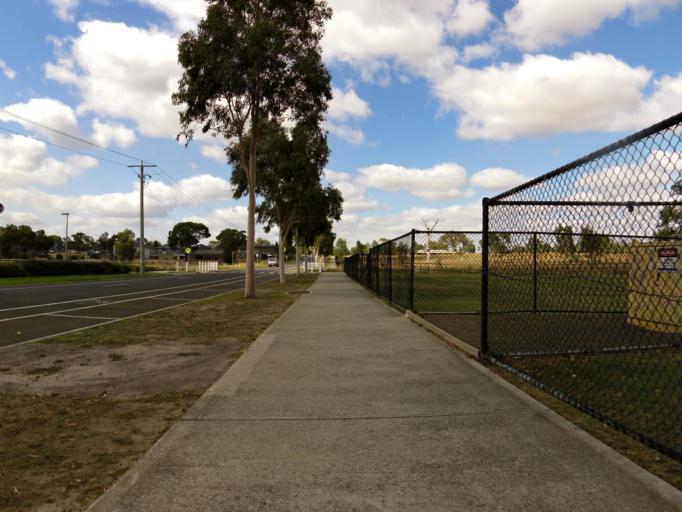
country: AU
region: Victoria
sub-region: Whittlesea
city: Mernda
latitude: -37.6302
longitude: 145.0780
